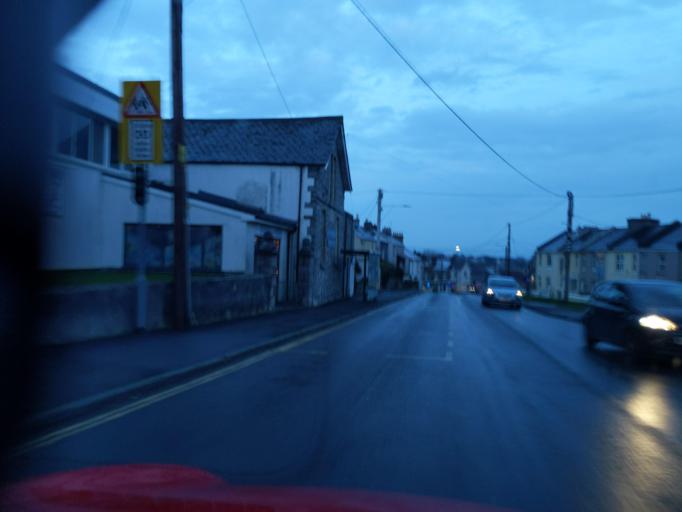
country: GB
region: England
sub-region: Plymouth
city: Plymstock
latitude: 50.3584
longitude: -4.0676
